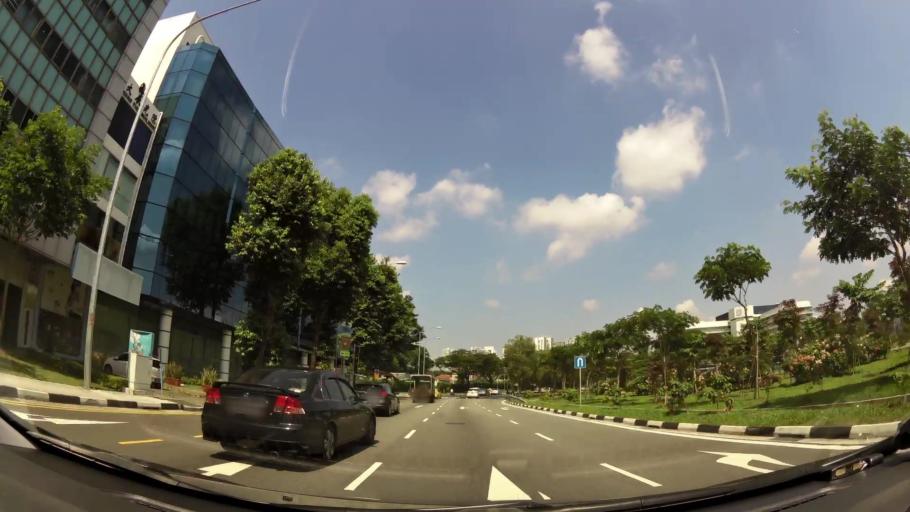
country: SG
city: Singapore
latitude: 1.3073
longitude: 103.8475
